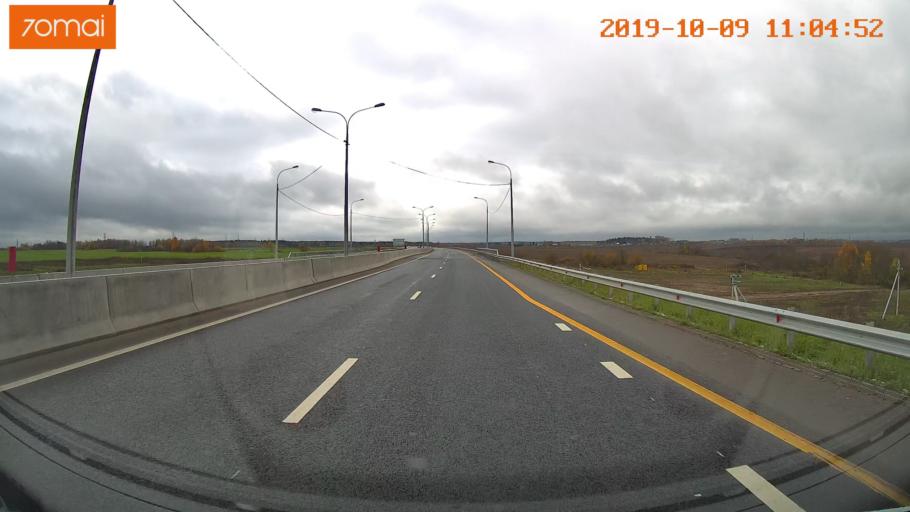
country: RU
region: Vologda
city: Molochnoye
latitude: 59.2070
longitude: 39.7626
